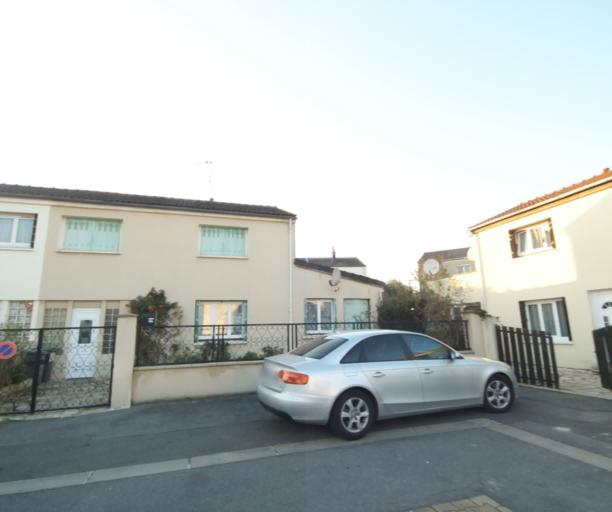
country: FR
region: Ile-de-France
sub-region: Departement du Val-d'Oise
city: Gonesse
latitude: 48.9870
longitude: 2.4353
